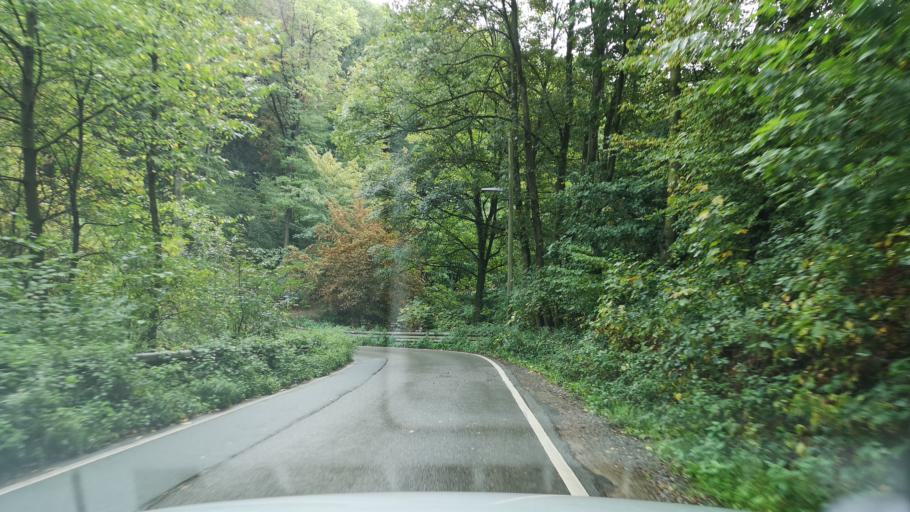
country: DE
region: North Rhine-Westphalia
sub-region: Regierungsbezirk Dusseldorf
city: Heiligenhaus
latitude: 51.3732
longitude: 6.9968
